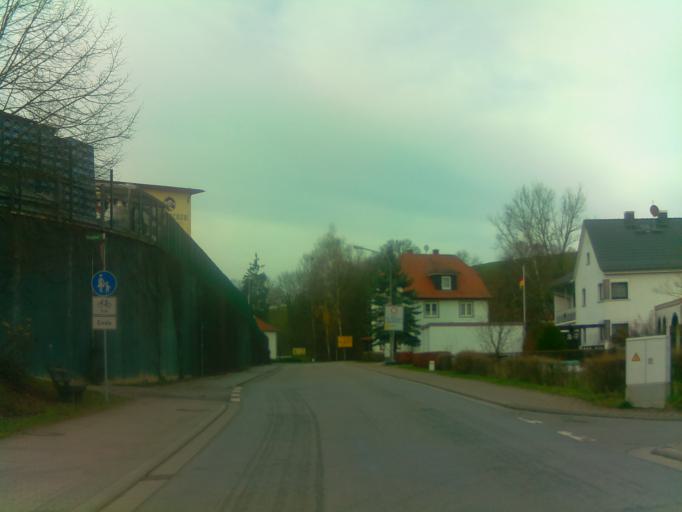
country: DE
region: Hesse
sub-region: Regierungsbezirk Darmstadt
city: Erbach
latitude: 49.6719
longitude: 8.9250
